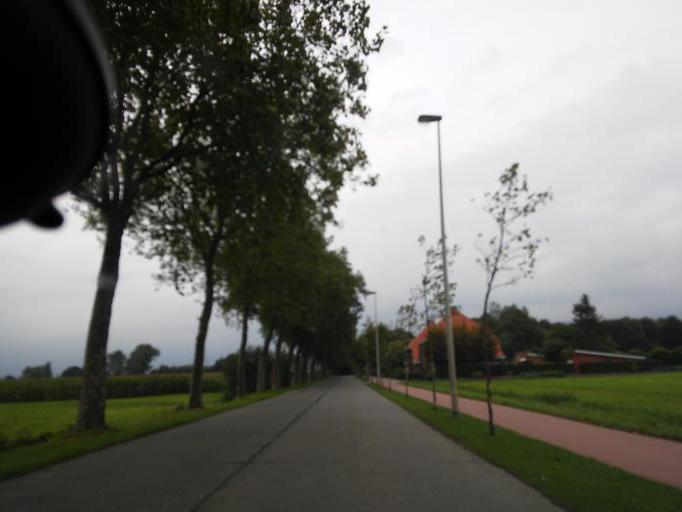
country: BE
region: Flanders
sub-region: Provincie Antwerpen
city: Rumst
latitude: 51.0951
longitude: 4.4182
